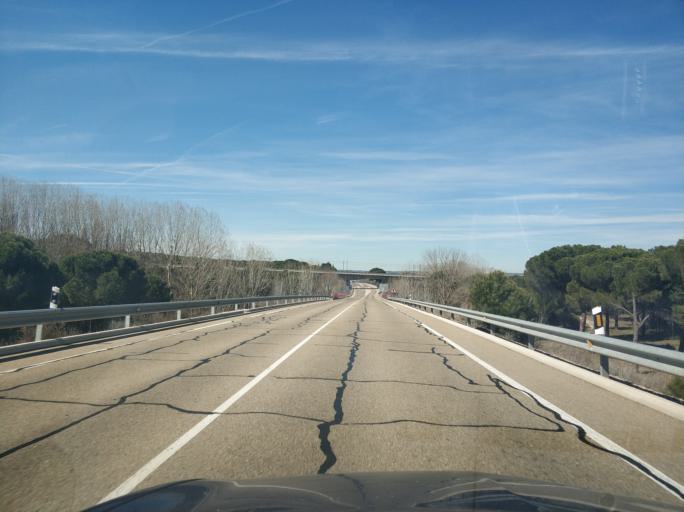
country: ES
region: Castille and Leon
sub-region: Provincia de Valladolid
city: Viana de Cega
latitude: 41.5349
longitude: -4.7587
